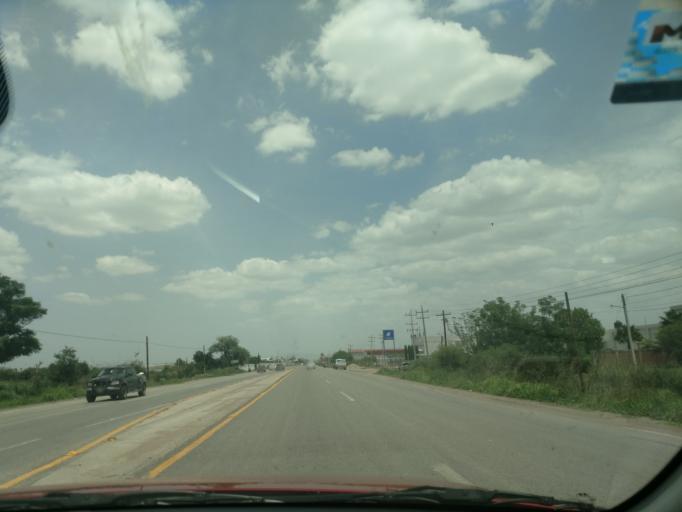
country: MX
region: San Luis Potosi
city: Ciudad Fernandez
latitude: 21.9416
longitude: -100.0412
